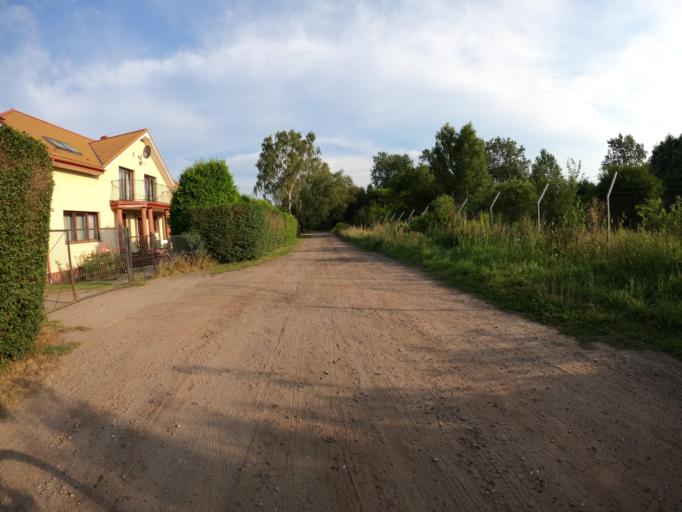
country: PL
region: West Pomeranian Voivodeship
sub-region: Koszalin
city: Koszalin
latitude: 54.1760
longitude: 16.2274
